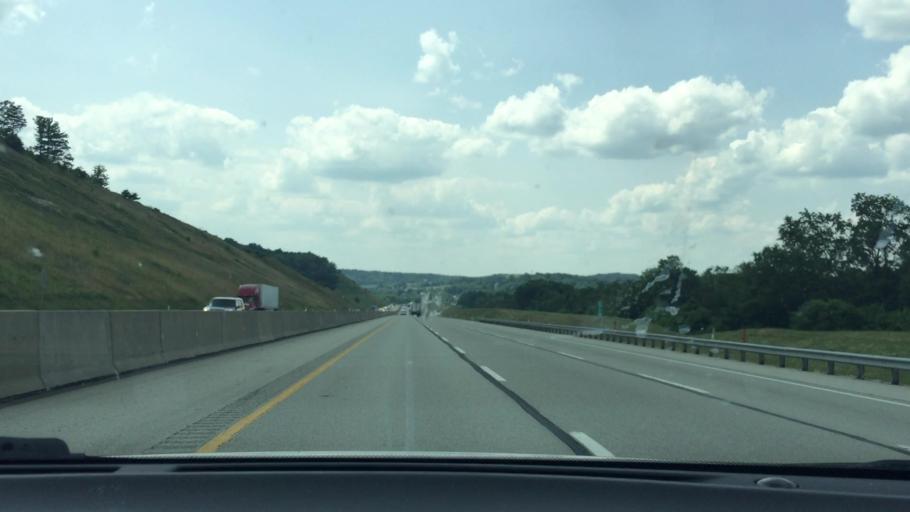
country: US
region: Pennsylvania
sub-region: Westmoreland County
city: New Stanton
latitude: 40.2628
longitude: -79.6489
